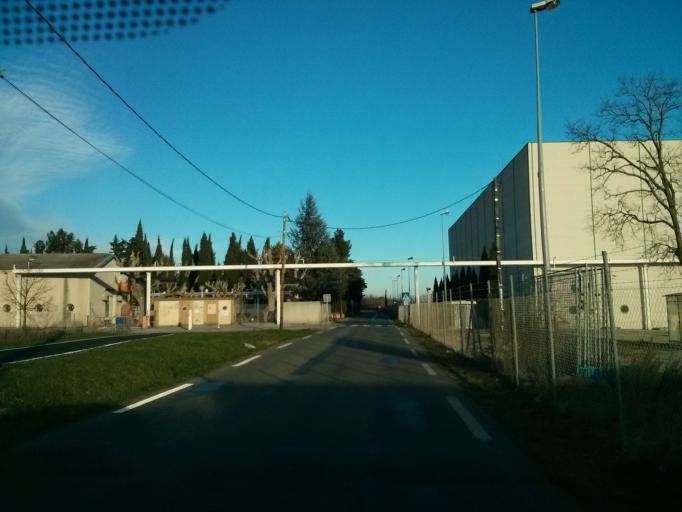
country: FR
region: Languedoc-Roussillon
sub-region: Departement du Gard
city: Mus
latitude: 43.7285
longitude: 4.1947
